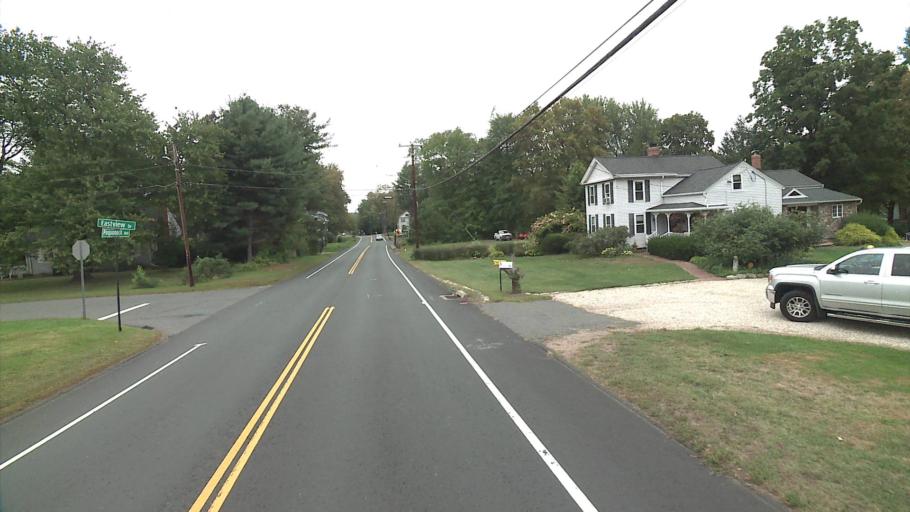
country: US
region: Connecticut
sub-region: Hartford County
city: Windsor
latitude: 41.8858
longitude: -72.6695
